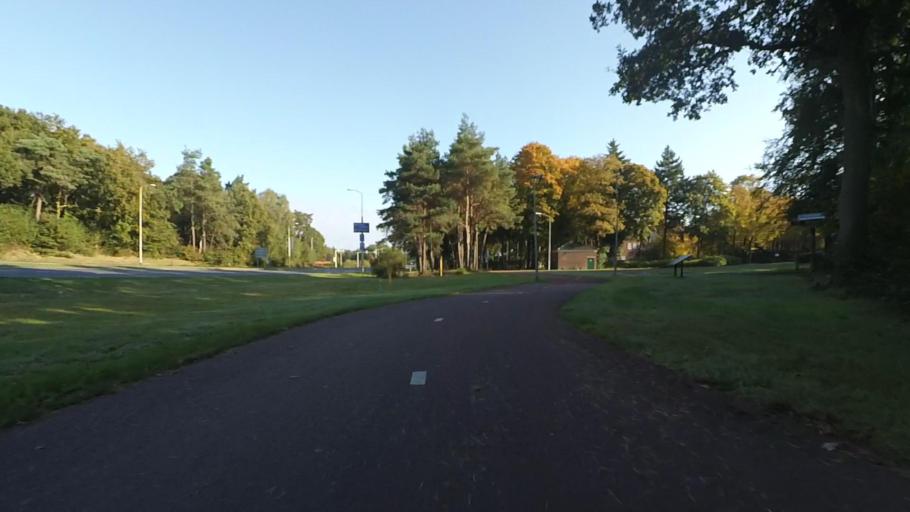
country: NL
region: Gelderland
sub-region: Gemeente Harderwijk
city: Harderwijk
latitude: 52.3332
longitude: 5.6411
